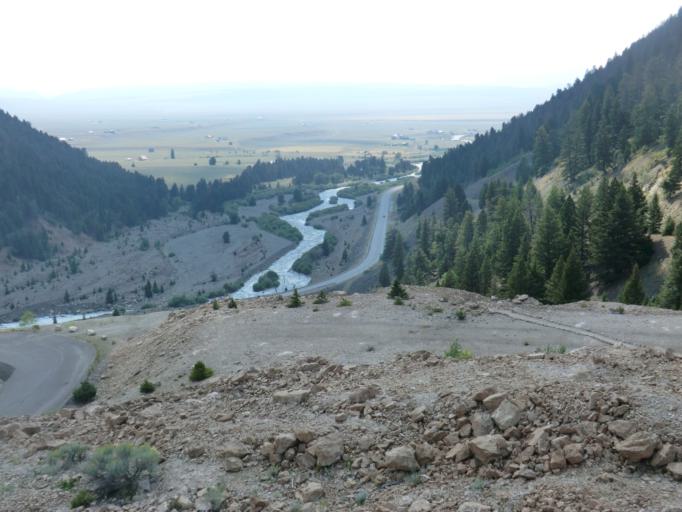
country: US
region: Montana
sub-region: Gallatin County
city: West Yellowstone
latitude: 44.8294
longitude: -111.4308
